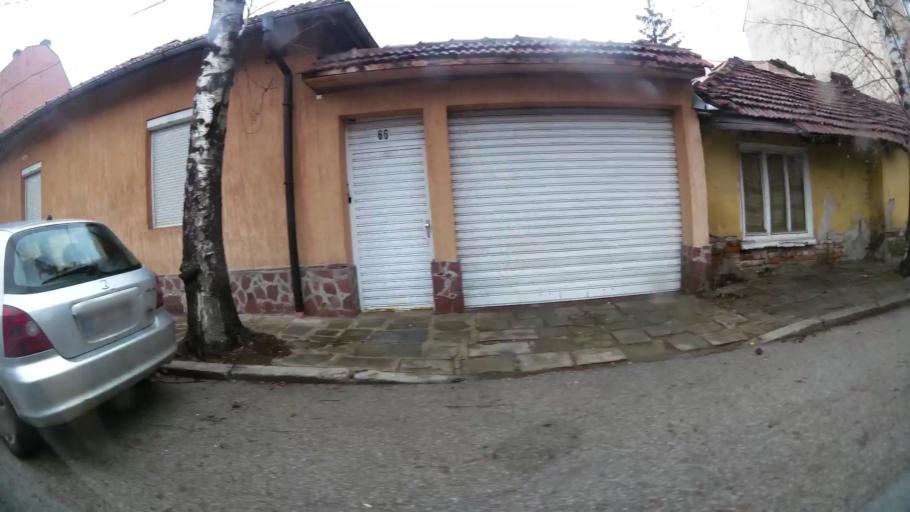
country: BG
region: Sofia-Capital
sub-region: Stolichna Obshtina
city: Sofia
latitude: 42.7296
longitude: 23.3011
